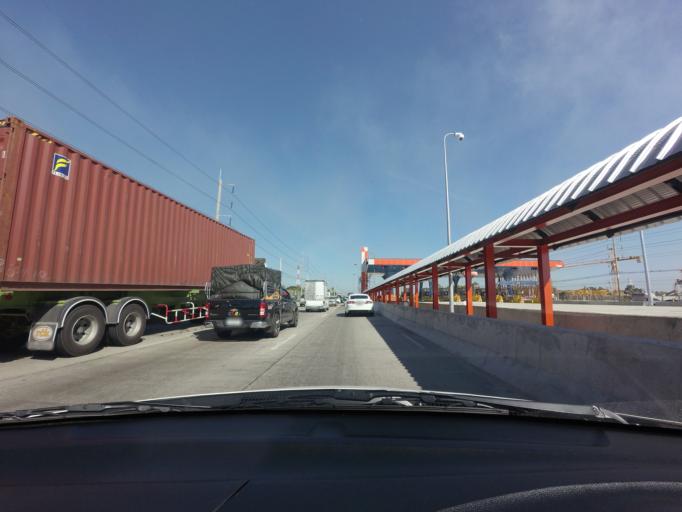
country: TH
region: Pathum Thani
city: Lam Luk Ka
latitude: 13.9661
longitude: 100.7128
